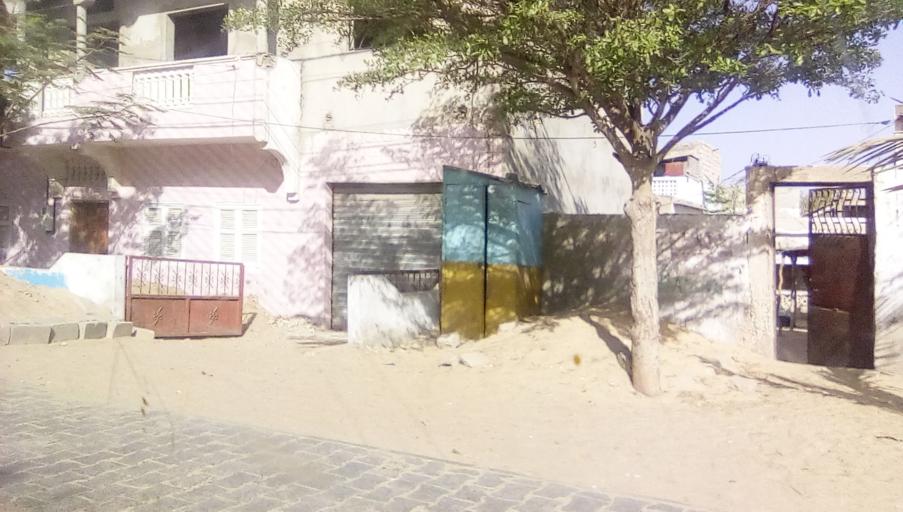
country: SN
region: Saint-Louis
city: Saint-Louis
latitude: 16.0315
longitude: -16.4723
